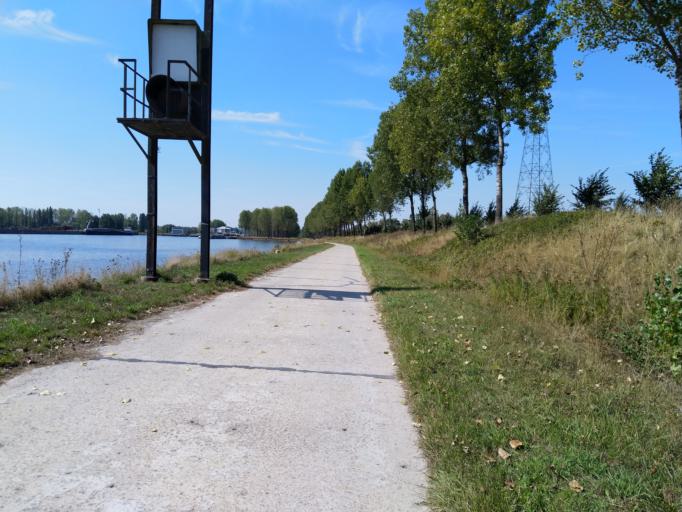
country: BE
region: Wallonia
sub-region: Province du Hainaut
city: Mons
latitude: 50.4770
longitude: 3.9897
